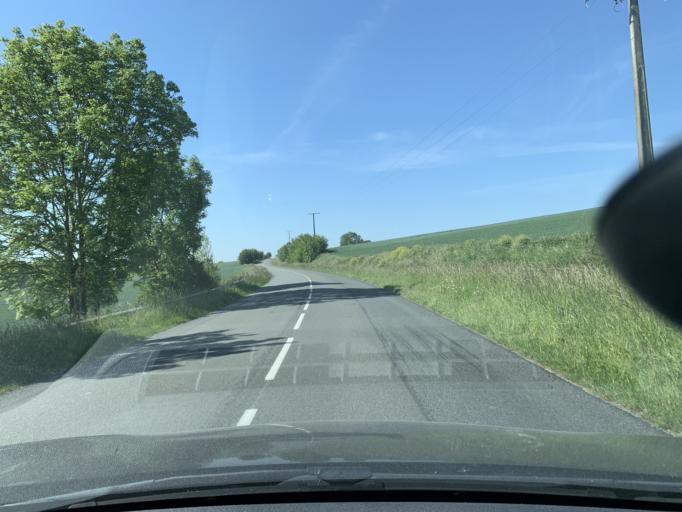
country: FR
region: Nord-Pas-de-Calais
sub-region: Departement du Nord
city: Masnieres
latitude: 50.0833
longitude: 3.2178
